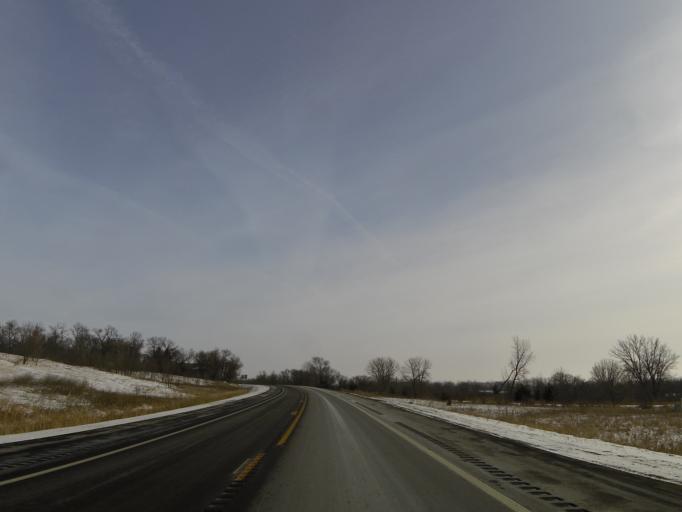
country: US
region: Minnesota
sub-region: McLeod County
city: Hutchinson
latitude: 44.8943
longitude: -94.4258
